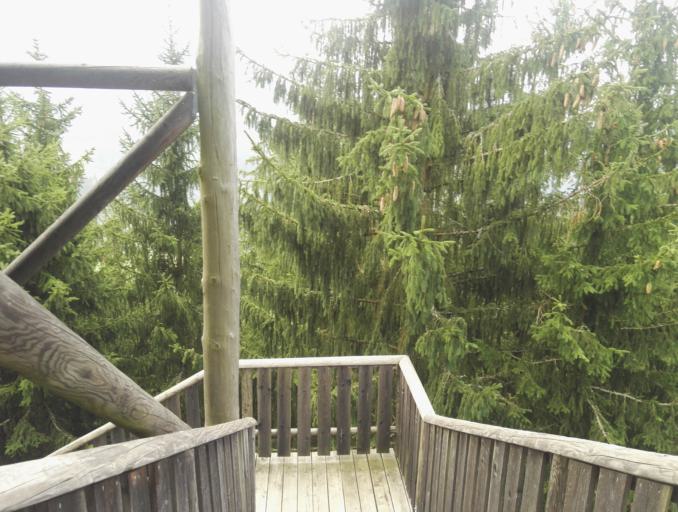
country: AT
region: Styria
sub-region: Politischer Bezirk Murtal
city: Sankt Margarethen bei Knittelfeld
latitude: 47.2151
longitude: 14.8693
